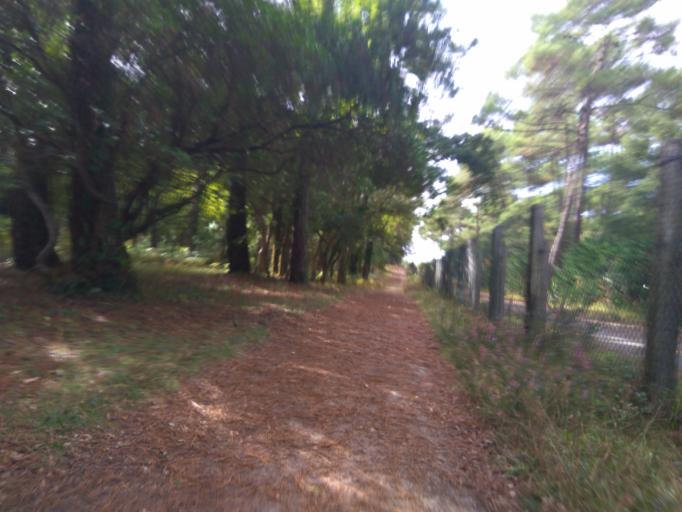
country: FR
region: Aquitaine
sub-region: Departement des Landes
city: Capbreton
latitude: 43.6285
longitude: -1.4463
